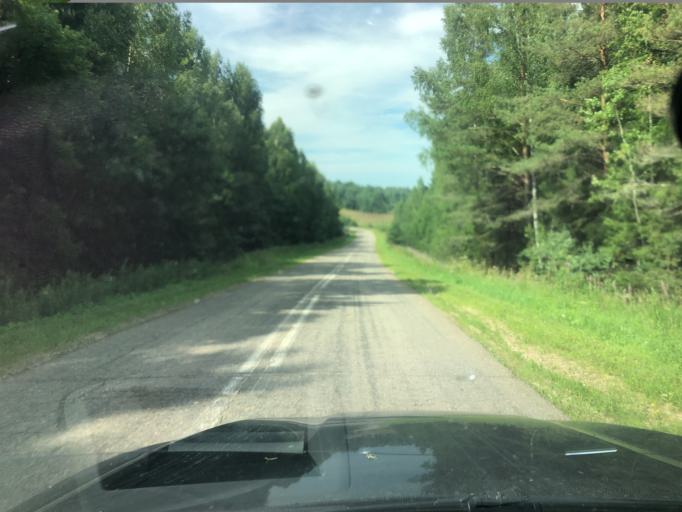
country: RU
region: Jaroslavl
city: Pereslavl'-Zalesskiy
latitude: 57.0335
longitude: 38.9092
